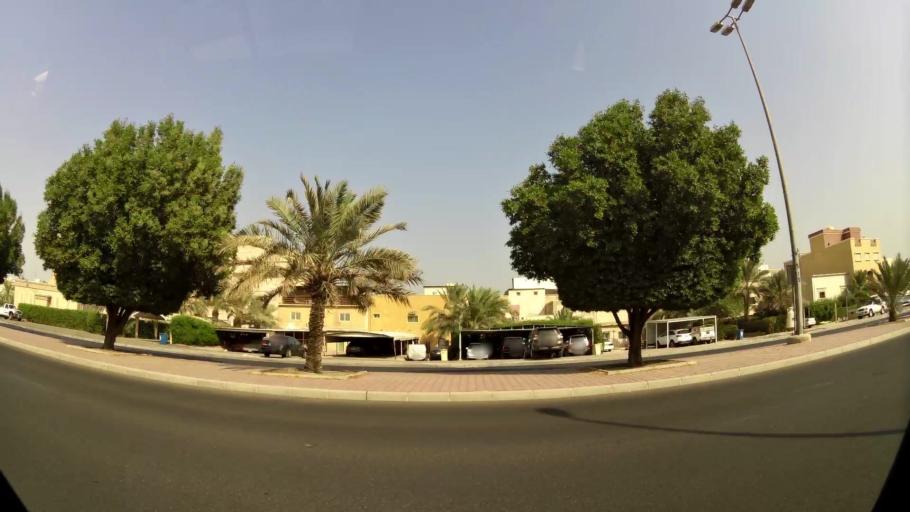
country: KW
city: Bayan
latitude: 29.2896
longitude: 48.0504
